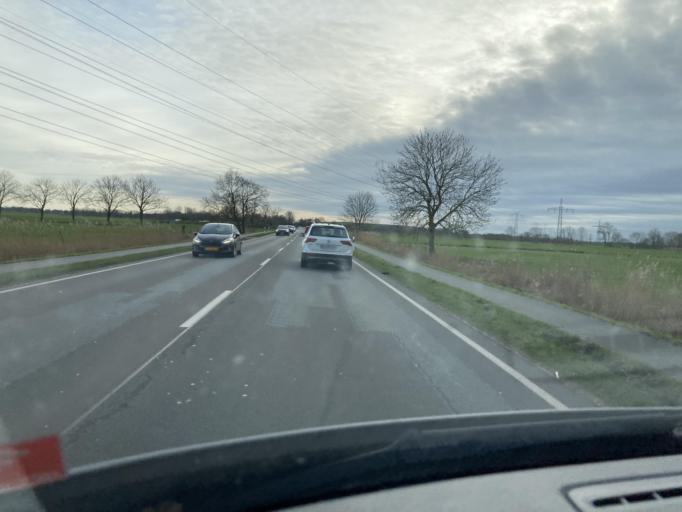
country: DE
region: Lower Saxony
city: Leer
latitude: 53.2129
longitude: 7.4834
